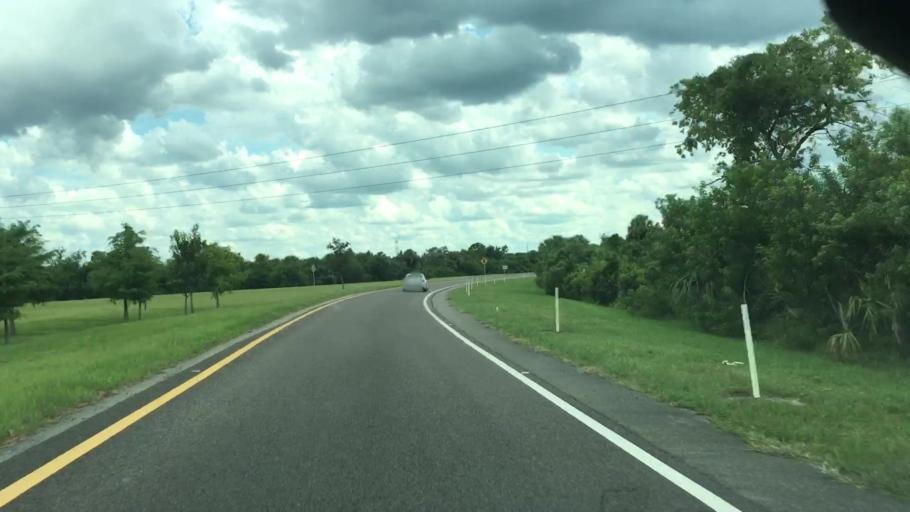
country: US
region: Florida
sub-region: Brevard County
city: Port Saint John
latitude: 28.4985
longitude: -80.8418
